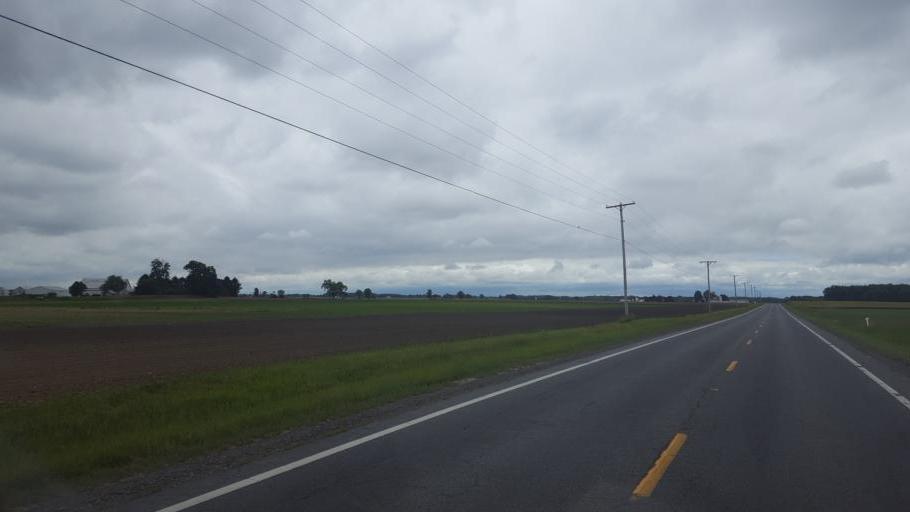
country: US
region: Ohio
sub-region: Crawford County
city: Bucyrus
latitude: 40.7770
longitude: -82.9231
